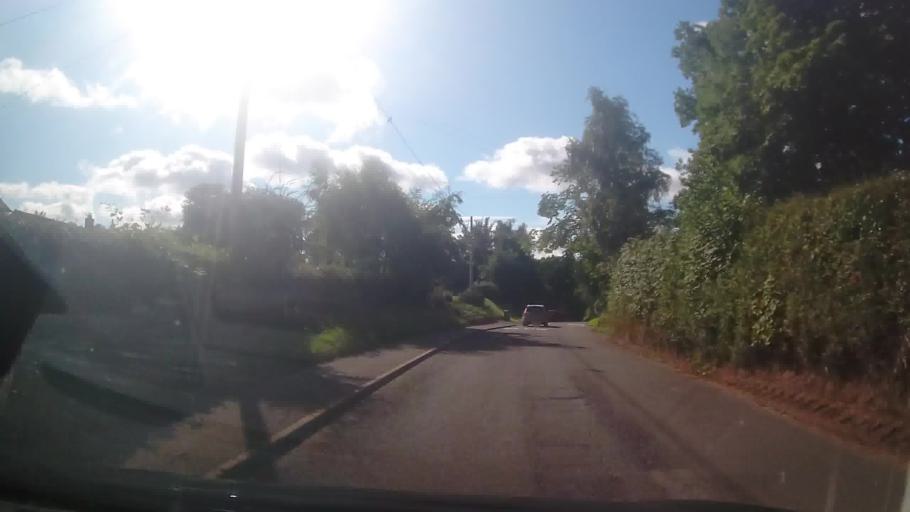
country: GB
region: England
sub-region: Shropshire
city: Ford
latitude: 52.7364
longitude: -2.8443
